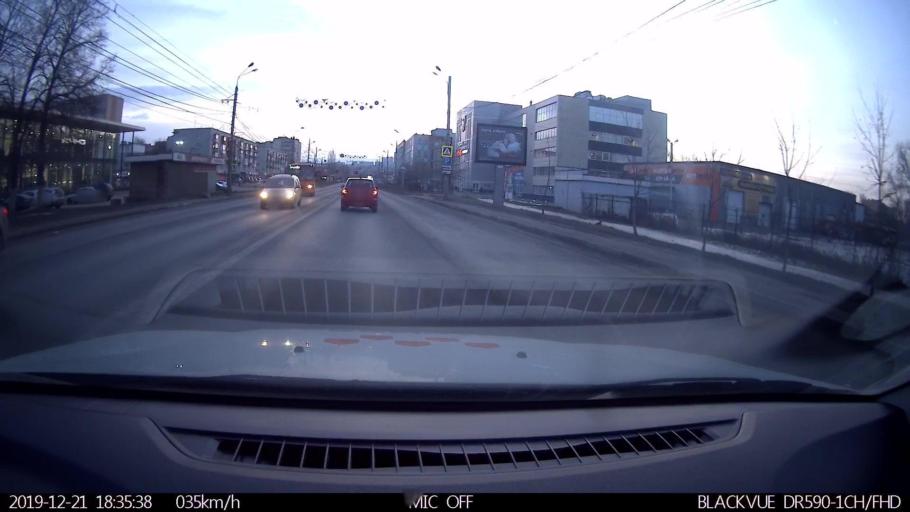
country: RU
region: Nizjnij Novgorod
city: Nizhniy Novgorod
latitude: 56.3220
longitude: 43.9222
